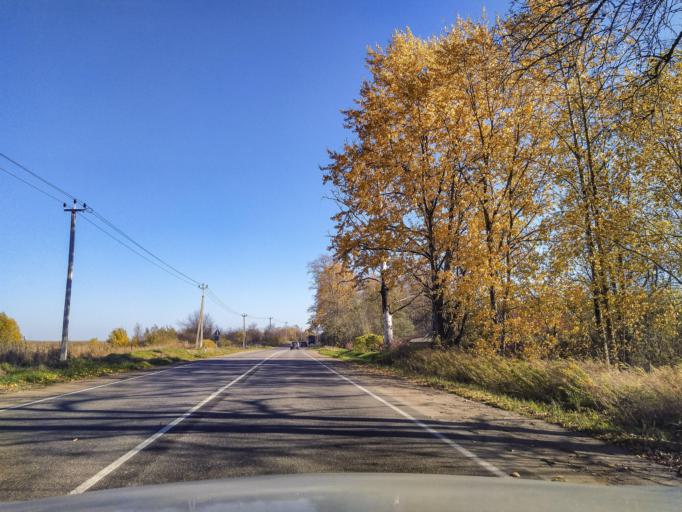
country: RU
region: Leningrad
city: Rozhdestveno
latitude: 59.3465
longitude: 29.9698
